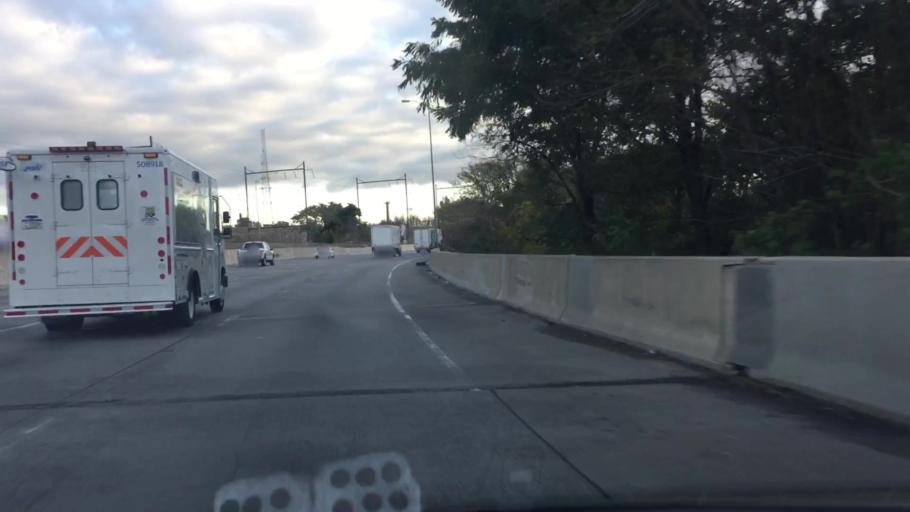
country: US
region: New Jersey
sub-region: Burlington County
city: Riverton
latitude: 40.0333
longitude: -75.0202
